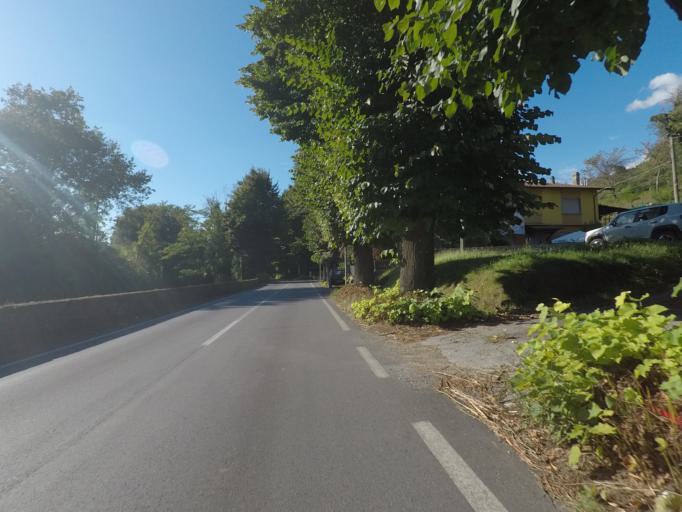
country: IT
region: Tuscany
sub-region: Provincia di Lucca
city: Corsanico-Bargecchia
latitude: 43.9242
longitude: 10.3256
